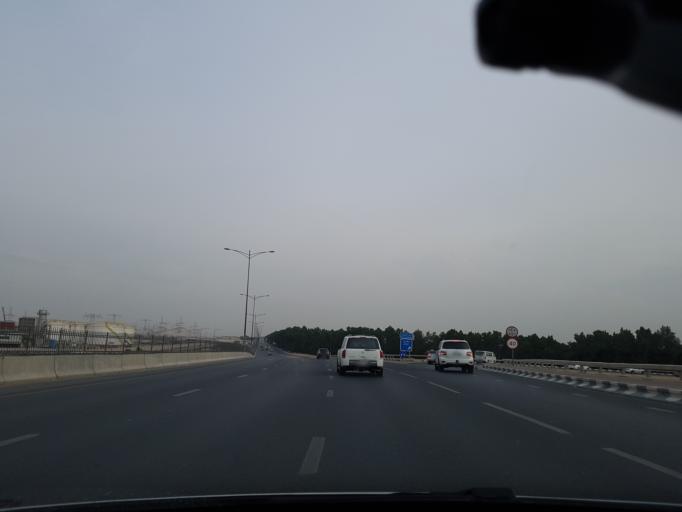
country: AE
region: Ajman
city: Ajman
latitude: 25.3728
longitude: 55.4553
